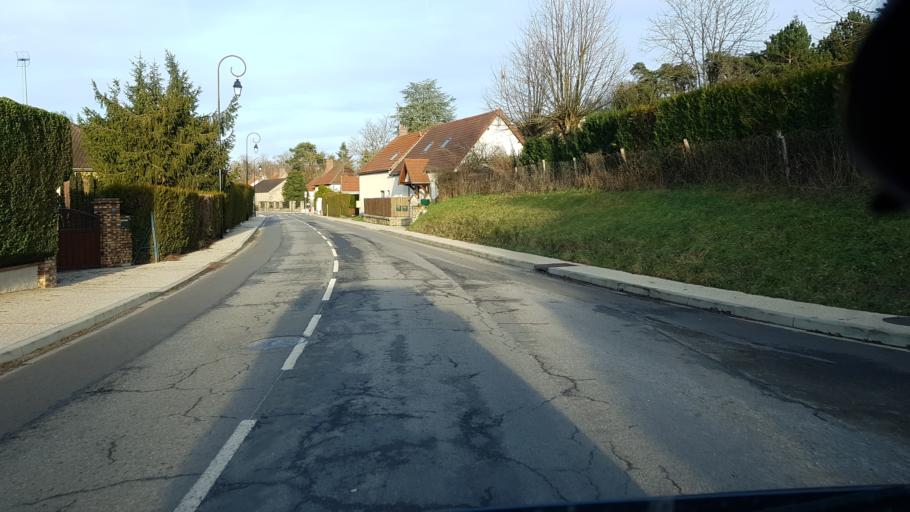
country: FR
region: Ile-de-France
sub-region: Departement des Yvelines
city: Gazeran
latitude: 48.6739
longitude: 1.7509
